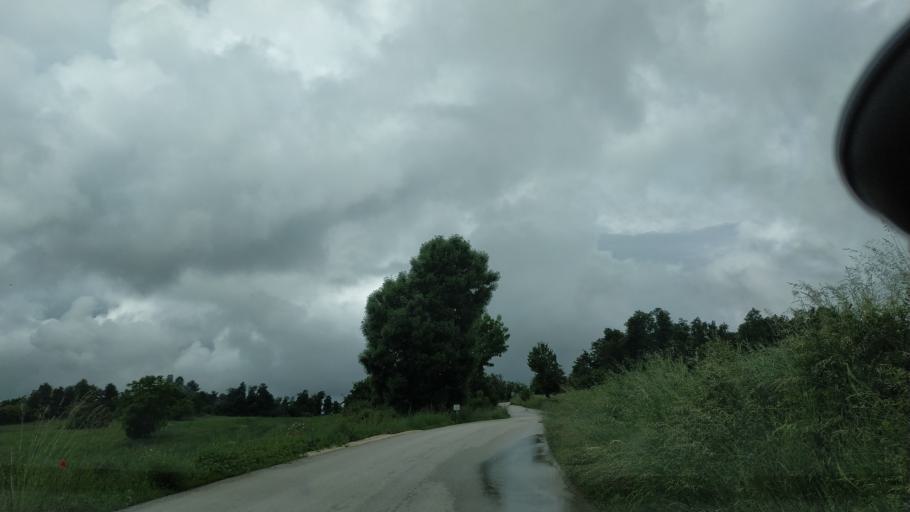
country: RS
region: Central Serbia
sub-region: Zajecarski Okrug
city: Soko Banja
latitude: 43.6842
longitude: 21.9332
